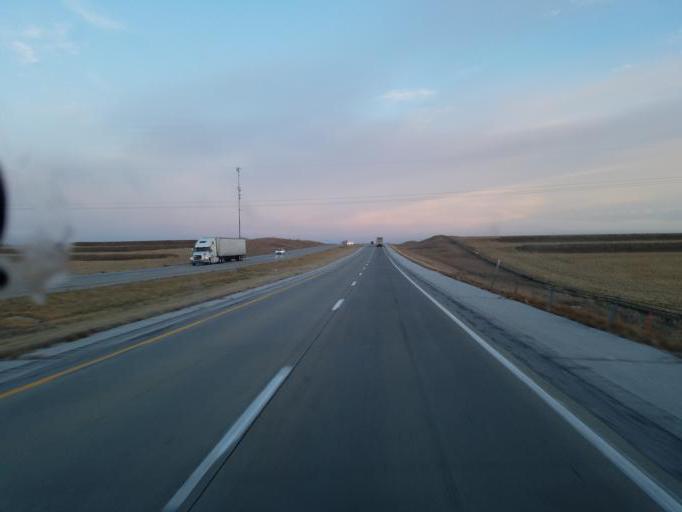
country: US
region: Iowa
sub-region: Pottawattamie County
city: Avoca
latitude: 41.4990
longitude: -95.4711
